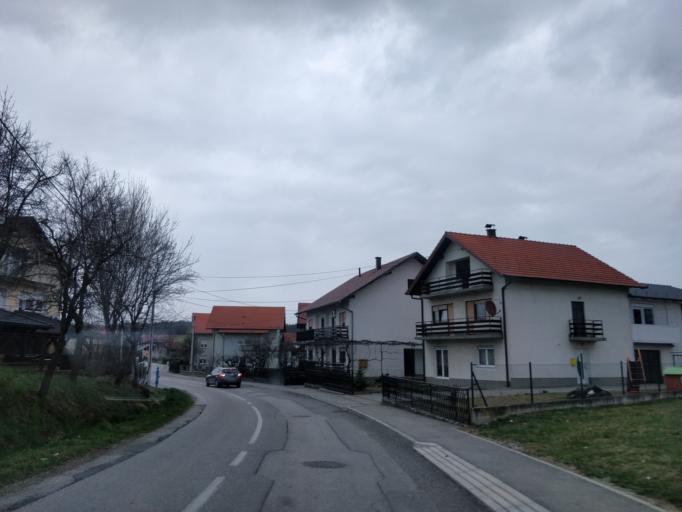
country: HR
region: Zagrebacka
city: Jakovlje
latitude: 45.9212
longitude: 15.9004
